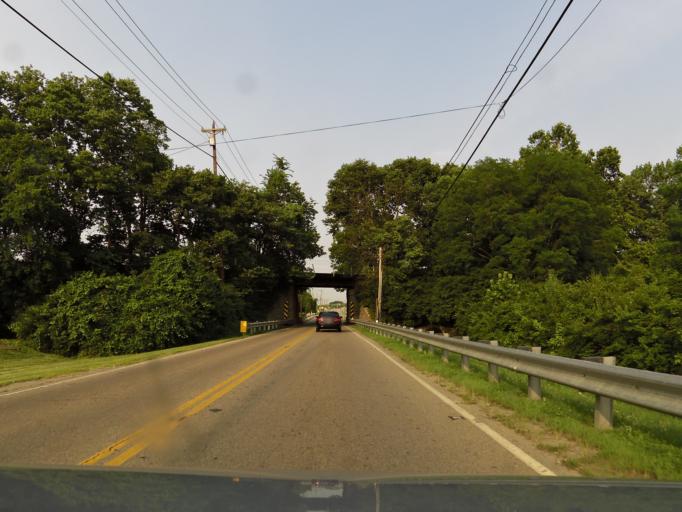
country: US
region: Ohio
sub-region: Hamilton County
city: Forest Park
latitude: 39.3343
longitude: -84.5110
